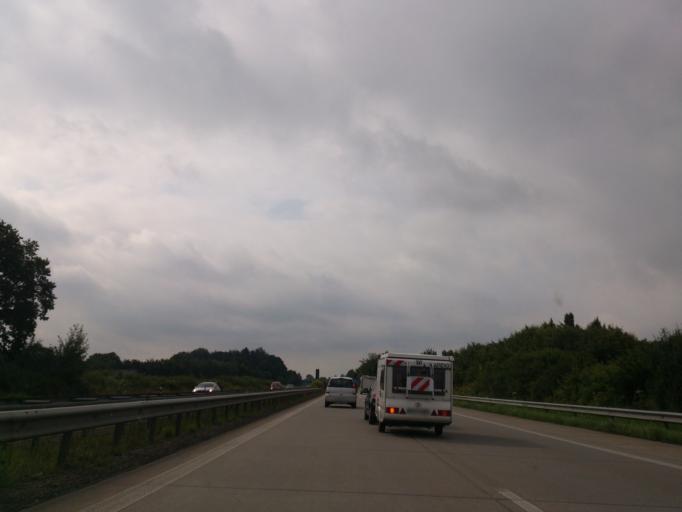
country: DE
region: Schleswig-Holstein
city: Kolln-Reisiek
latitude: 53.7505
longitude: 9.7102
